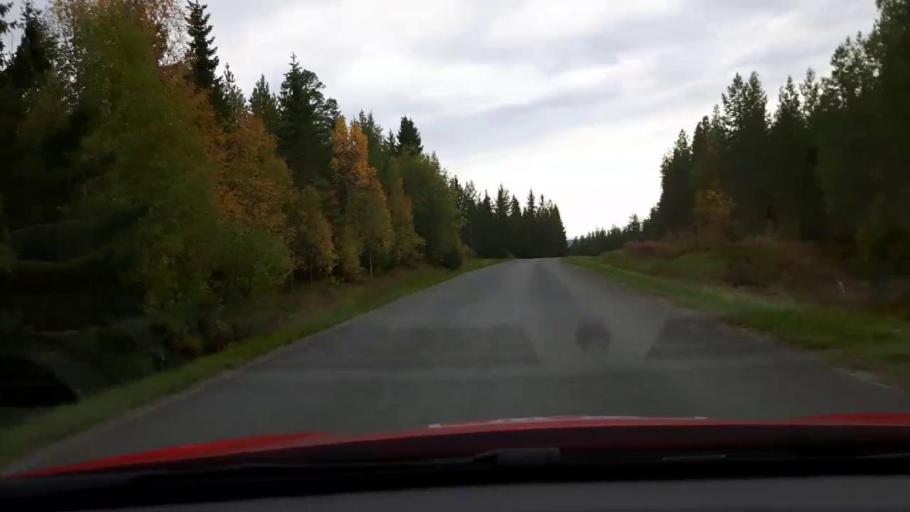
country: SE
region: Jaemtland
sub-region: Krokoms Kommun
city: Krokom
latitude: 63.2150
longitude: 14.1192
